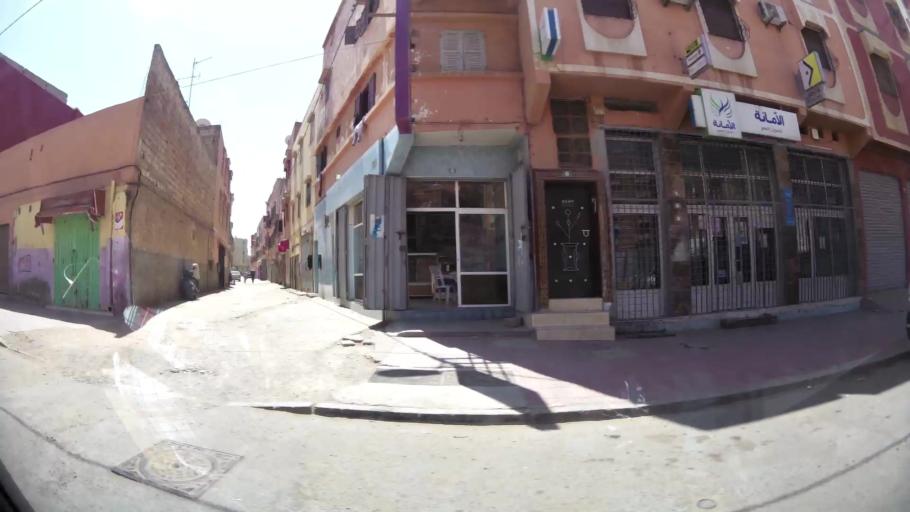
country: MA
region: Souss-Massa-Draa
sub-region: Inezgane-Ait Mellou
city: Inezgane
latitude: 30.3452
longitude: -9.4950
